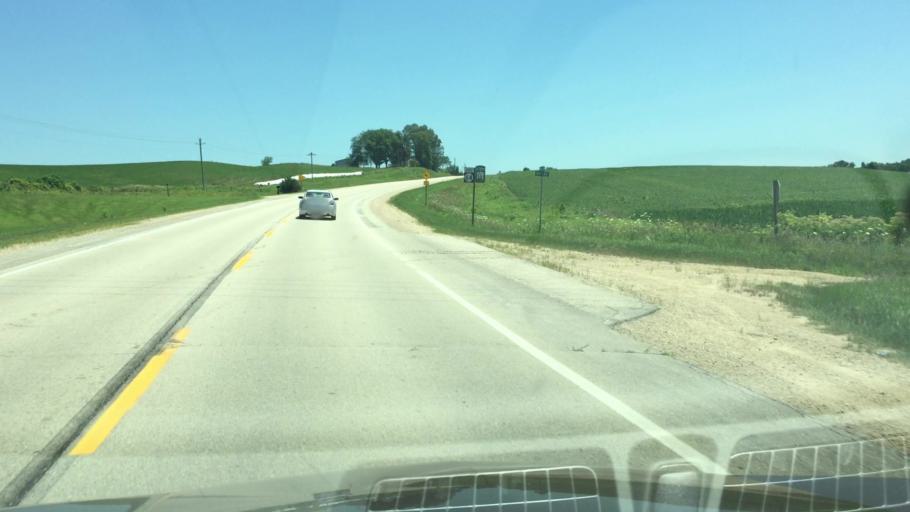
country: US
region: Iowa
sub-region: Jackson County
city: Maquoketa
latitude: 42.0727
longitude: -90.8009
